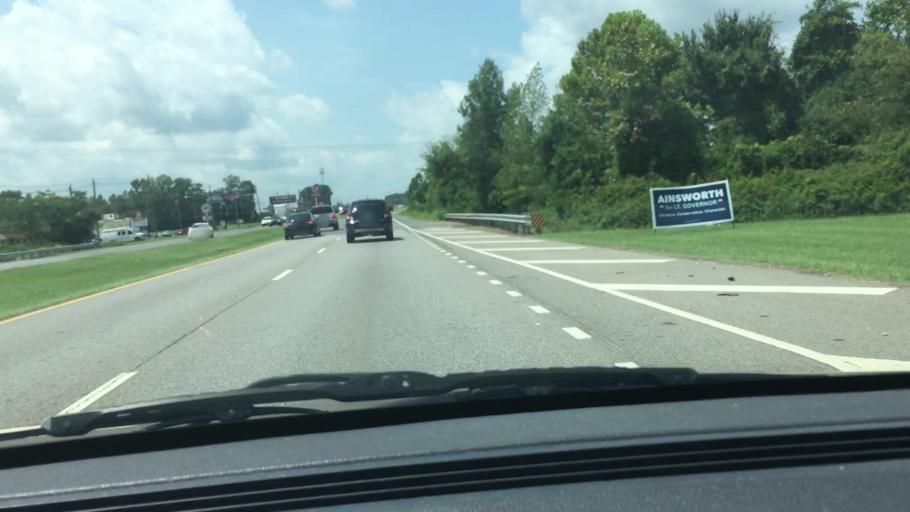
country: US
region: Alabama
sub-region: Tuscaloosa County
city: Northport
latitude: 33.2376
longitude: -87.6030
